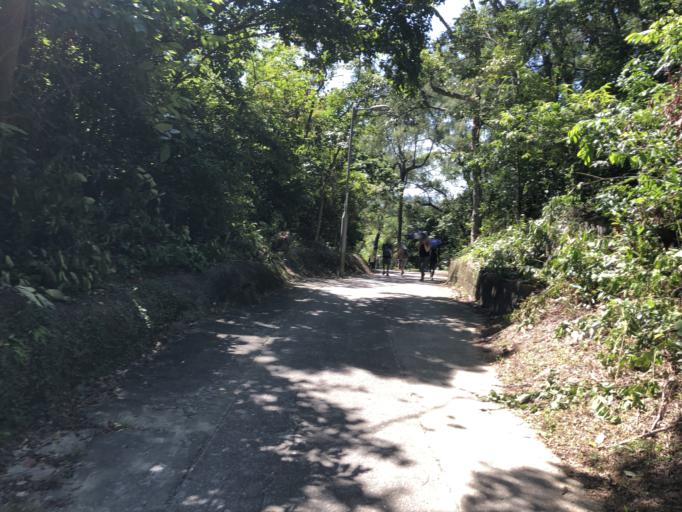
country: HK
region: Tuen Mun
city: Tuen Mun
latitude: 22.2939
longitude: 113.9739
